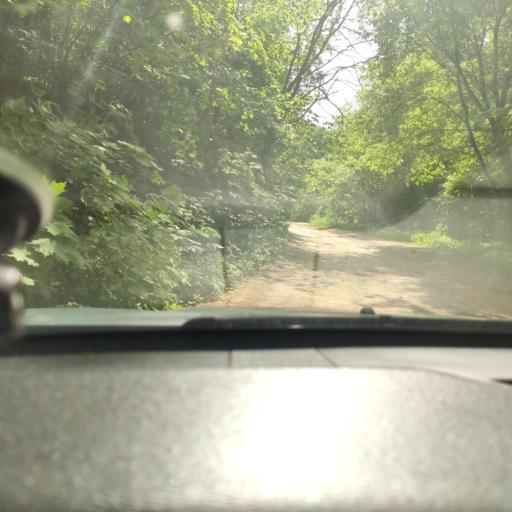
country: RU
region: Samara
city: Volzhskiy
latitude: 53.3385
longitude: 50.2107
